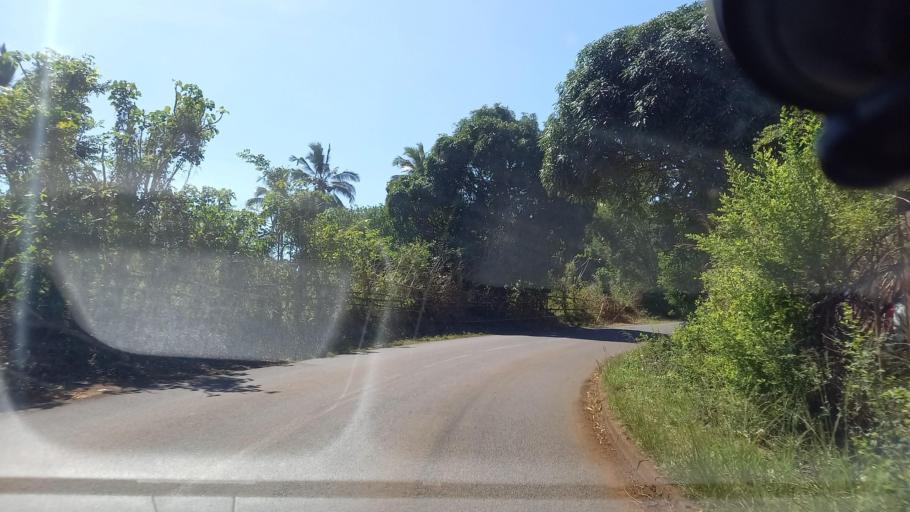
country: YT
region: Tsingoni
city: Tsingoni
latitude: -12.7845
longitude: 45.1417
